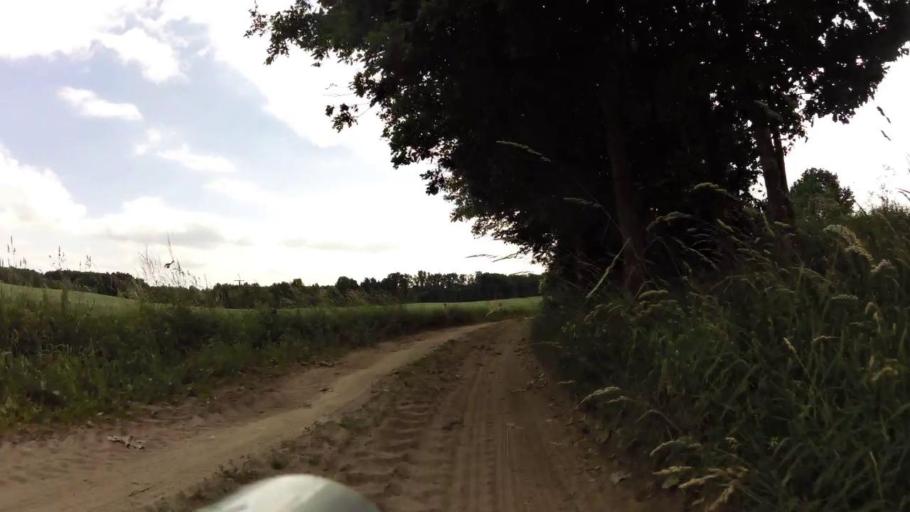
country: PL
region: West Pomeranian Voivodeship
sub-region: Powiat koszalinski
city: Bobolice
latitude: 53.9597
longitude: 16.6850
